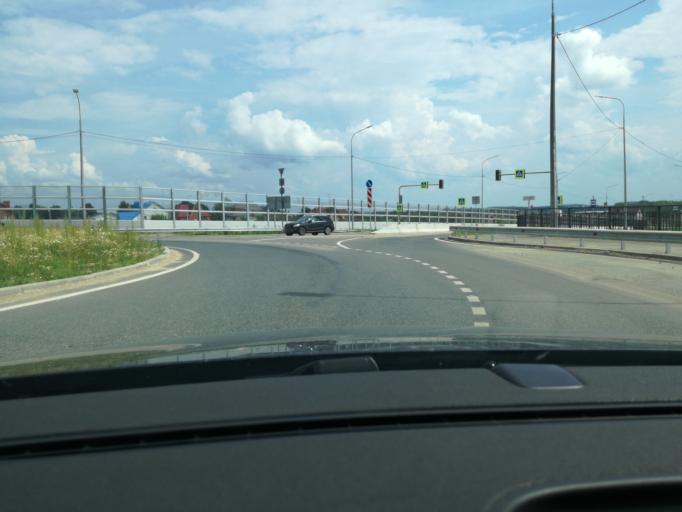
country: RU
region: Moskovskaya
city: Sergiyev Posad
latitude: 56.2922
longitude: 38.1049
